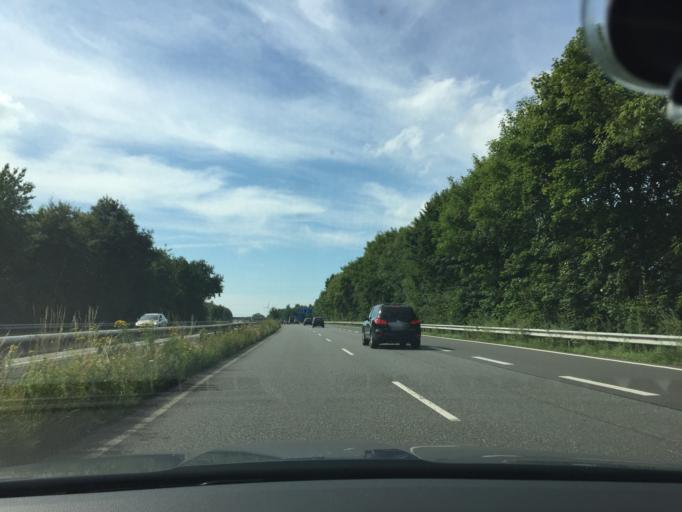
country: DE
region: Lower Saxony
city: Sande
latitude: 53.5224
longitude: 8.0167
